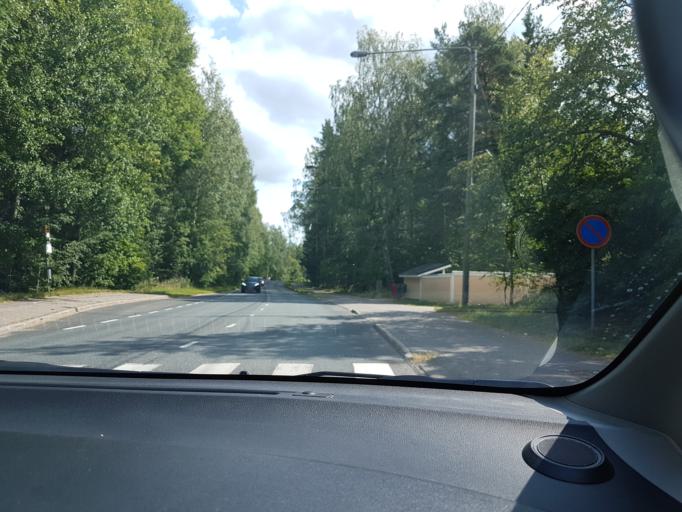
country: FI
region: Uusimaa
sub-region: Helsinki
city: Vantaa
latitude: 60.2604
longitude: 25.0973
